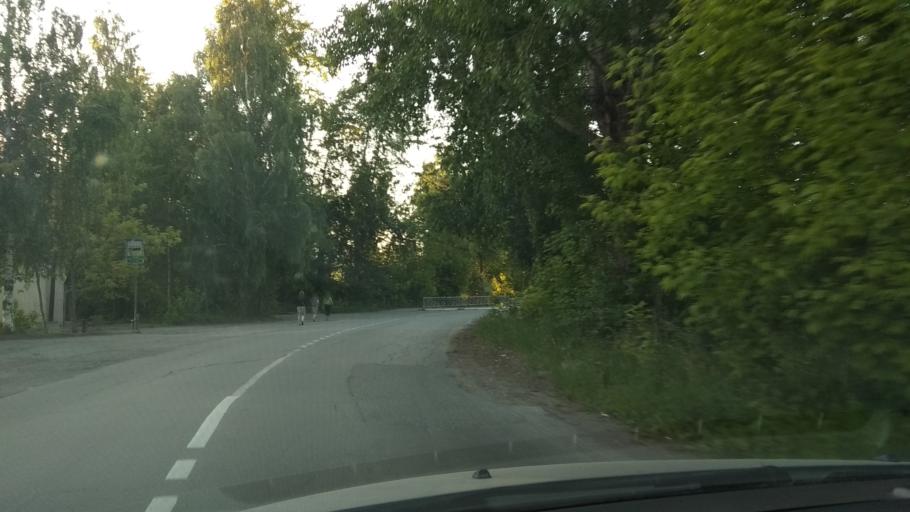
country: RU
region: Sverdlovsk
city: Sredneuralsk
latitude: 56.9829
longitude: 60.4601
